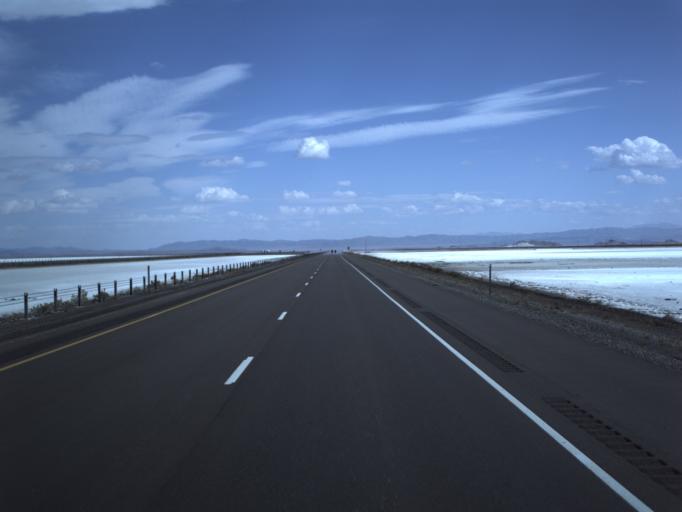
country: US
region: Utah
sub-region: Tooele County
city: Wendover
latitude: 40.7289
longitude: -113.4137
